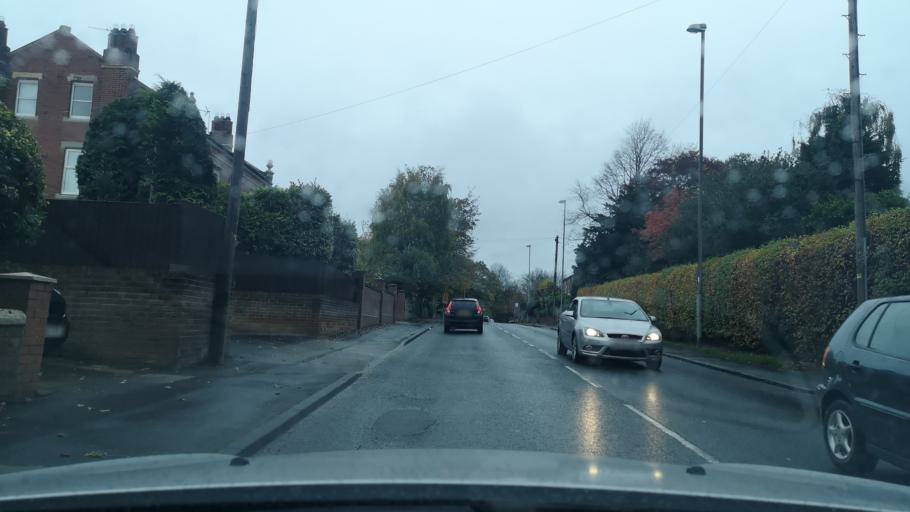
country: GB
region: England
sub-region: City and Borough of Wakefield
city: Pontefract
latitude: 53.6822
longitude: -1.3132
